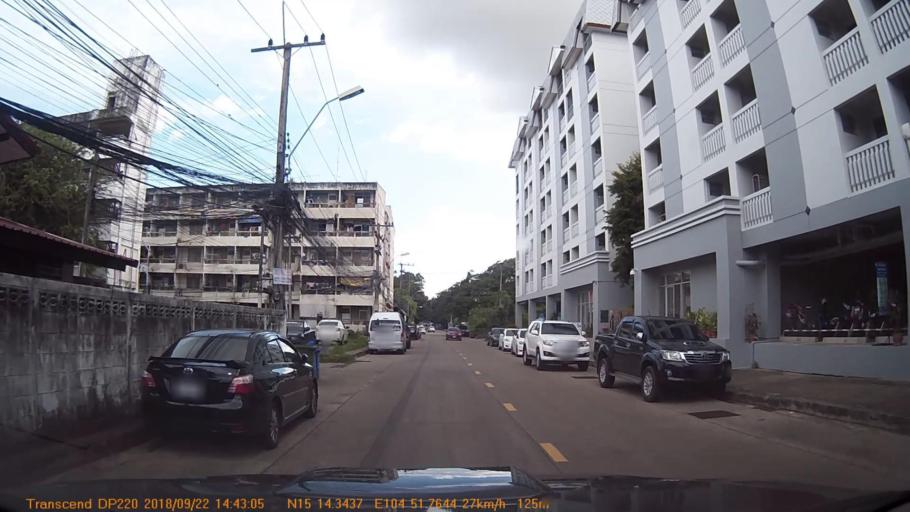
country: TH
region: Changwat Ubon Ratchathani
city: Ubon Ratchathani
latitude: 15.2388
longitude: 104.8628
